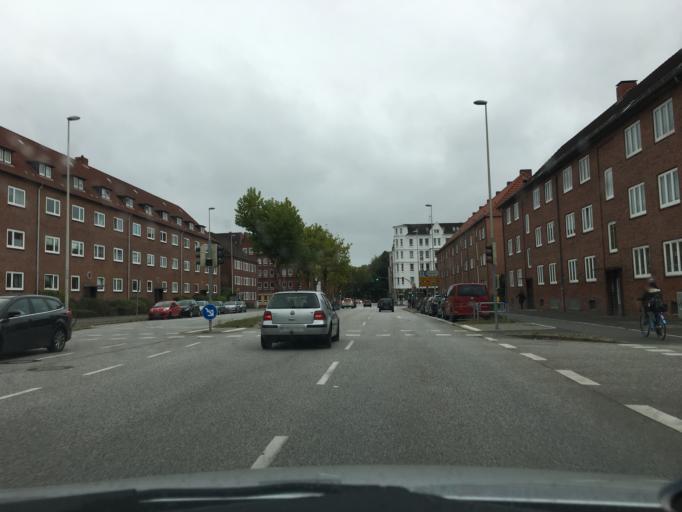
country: DE
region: Schleswig-Holstein
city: Kiel
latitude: 54.3255
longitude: 10.1117
